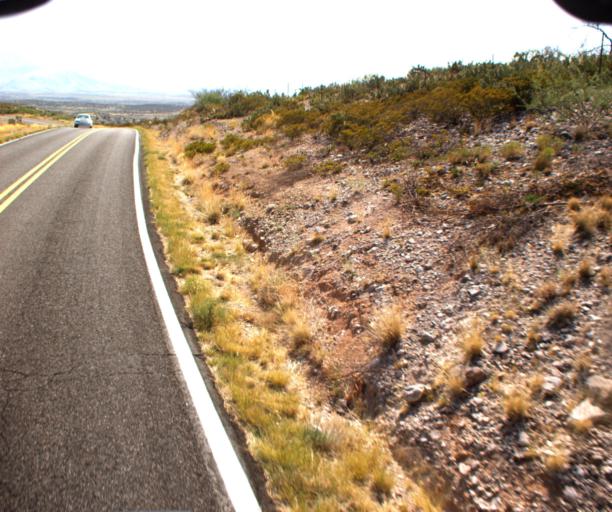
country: US
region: Arizona
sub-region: Greenlee County
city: Clifton
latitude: 32.9994
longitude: -109.1734
